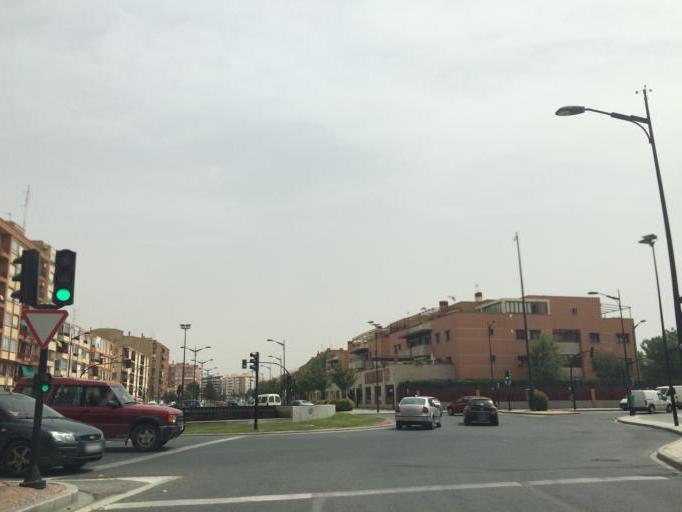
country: ES
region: Castille-La Mancha
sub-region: Provincia de Albacete
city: Albacete
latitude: 38.9851
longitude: -1.8640
